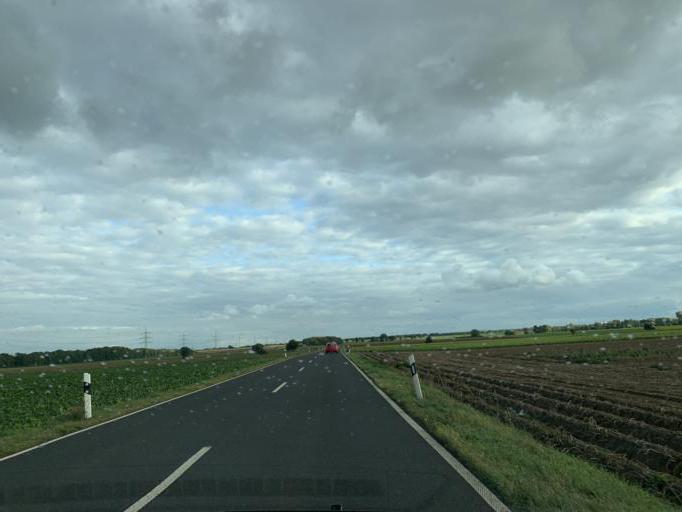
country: DE
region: North Rhine-Westphalia
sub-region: Regierungsbezirk Koln
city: Aldenhoven
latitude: 50.9288
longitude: 6.2960
